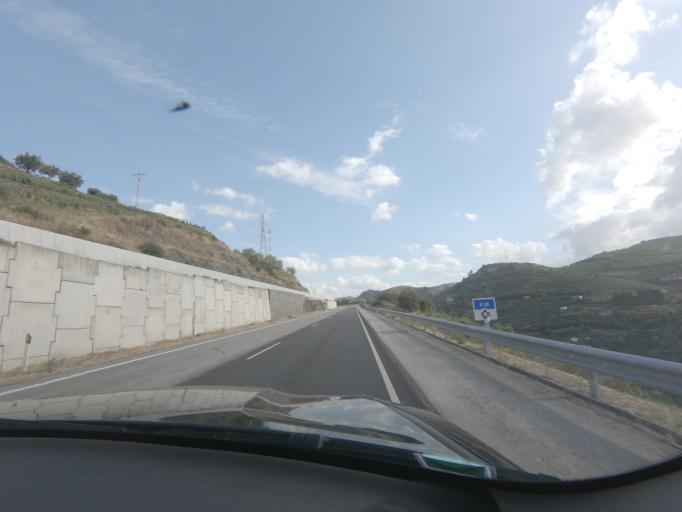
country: PT
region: Vila Real
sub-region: Peso da Regua
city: Peso da Regua
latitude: 41.1464
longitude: -7.7748
